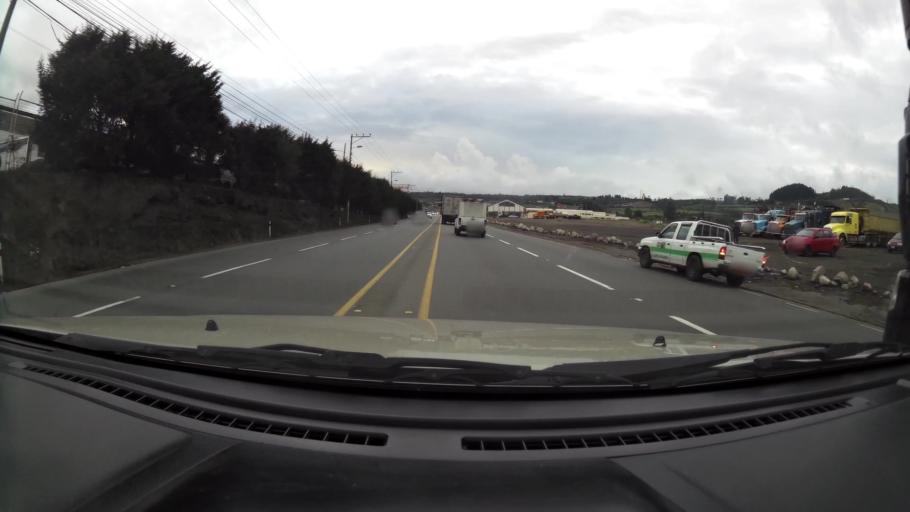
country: EC
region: Pichincha
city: Machachi
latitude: -0.4487
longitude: -78.6361
